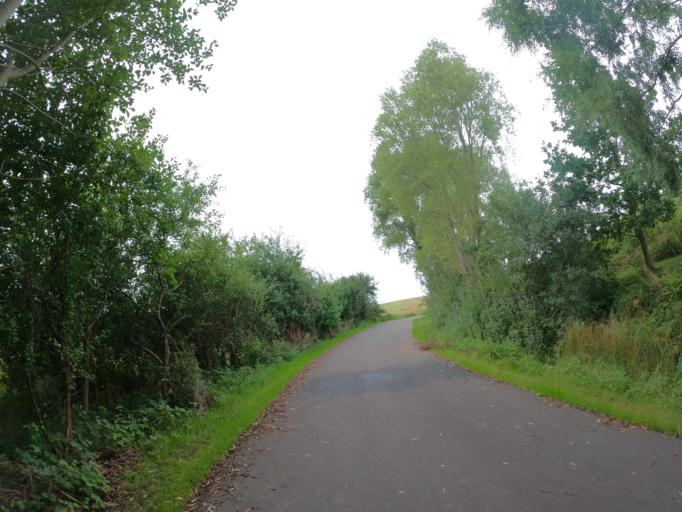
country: DE
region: Mecklenburg-Vorpommern
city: Rambin
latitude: 54.3029
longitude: 13.2030
